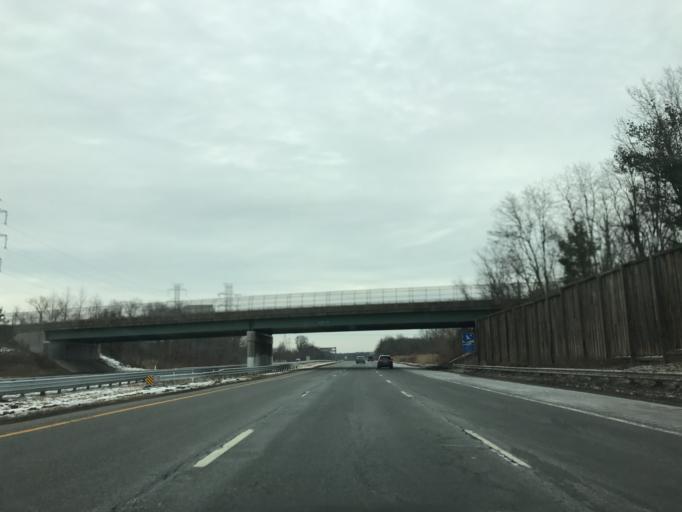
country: US
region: New Jersey
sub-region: Mercer County
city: White Horse
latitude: 40.2109
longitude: -74.7055
